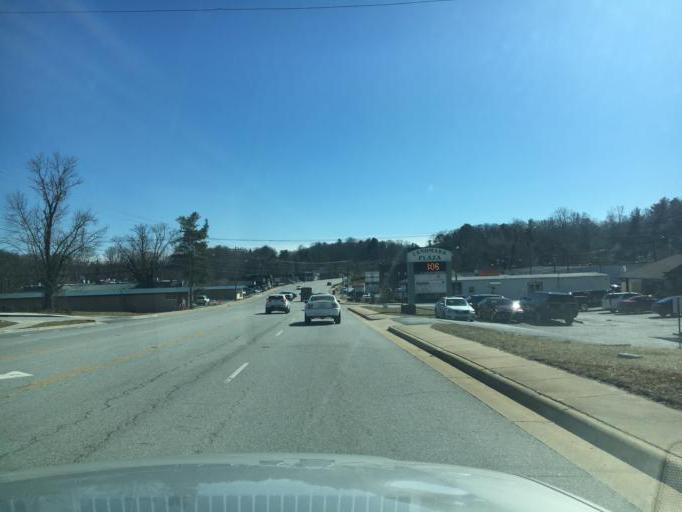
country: US
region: North Carolina
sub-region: Henderson County
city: Balfour
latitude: 35.3358
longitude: -82.4721
